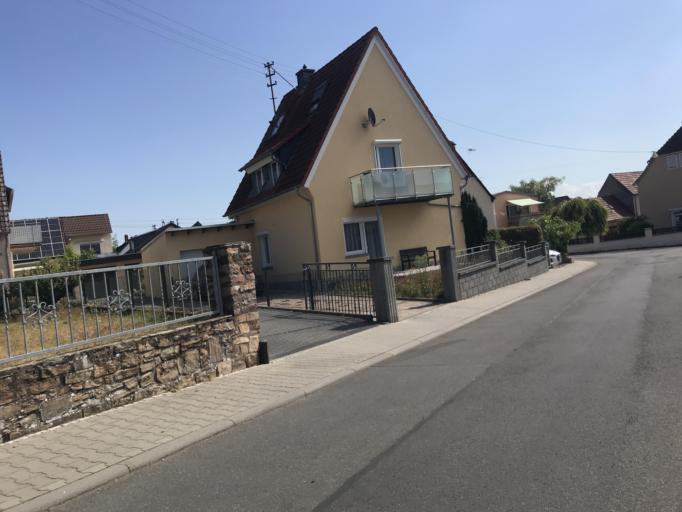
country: DE
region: Rheinland-Pfalz
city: Oestrich-Winkel
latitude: 50.0001
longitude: 8.0030
